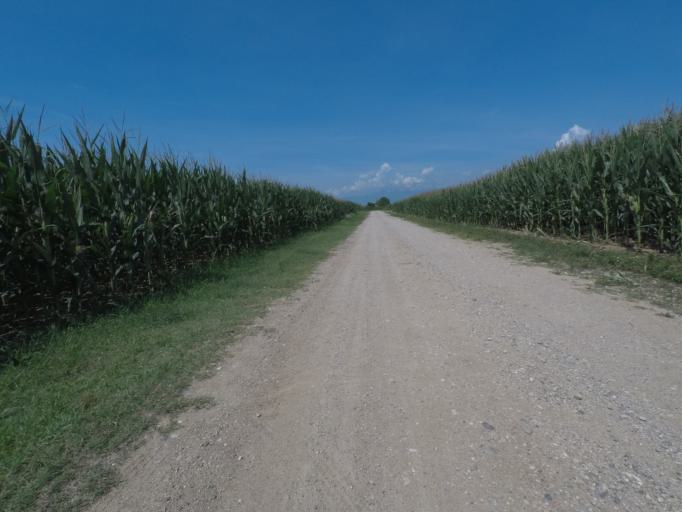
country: IT
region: Friuli Venezia Giulia
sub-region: Provincia di Udine
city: Dignano
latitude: 46.0838
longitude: 12.9512
